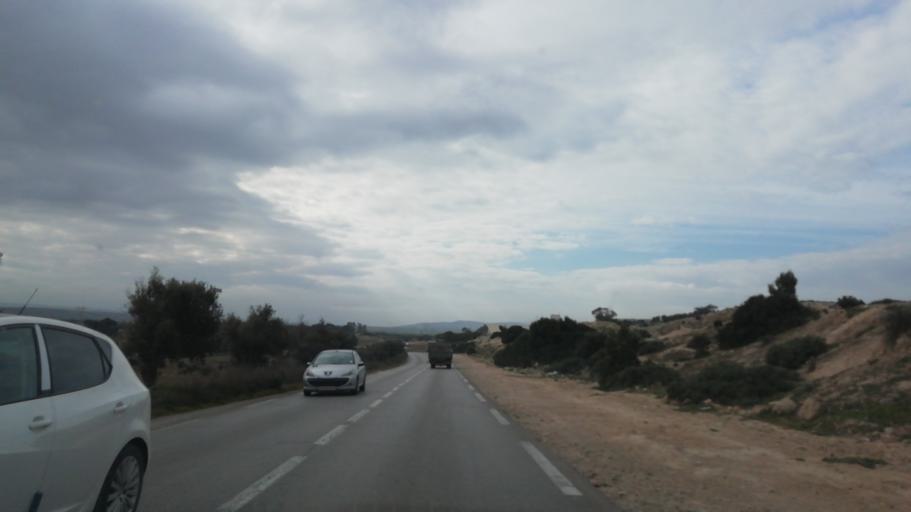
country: DZ
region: Oran
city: Ain el Bya
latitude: 35.7166
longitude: -0.3587
